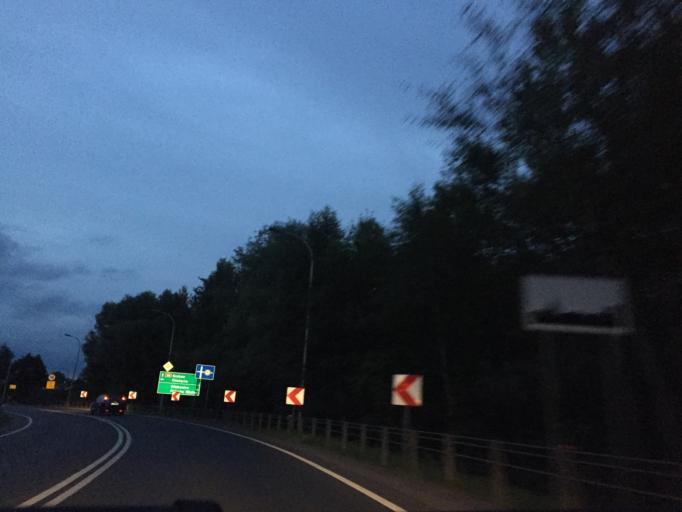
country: PL
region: Lesser Poland Voivodeship
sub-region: Powiat oswiecimski
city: Zaborze
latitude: 50.0235
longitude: 19.2521
